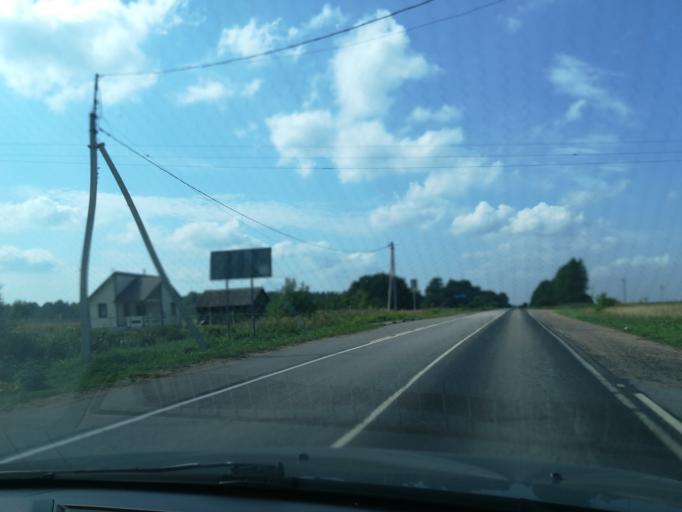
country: RU
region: Leningrad
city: Kopor'ye
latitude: 59.6331
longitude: 28.9715
